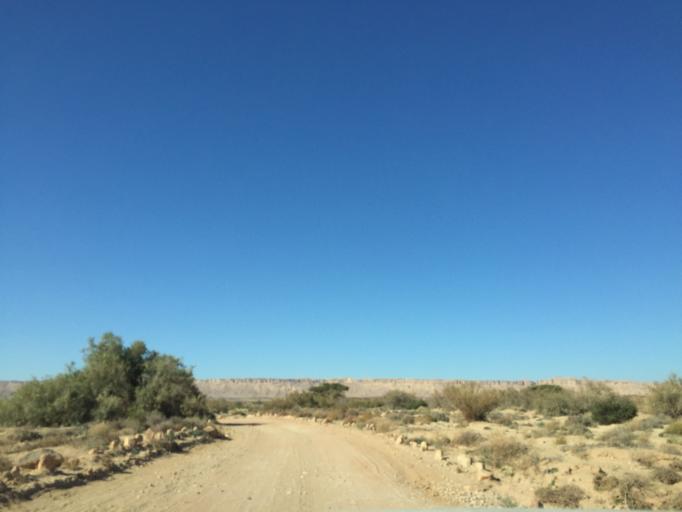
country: IL
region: Southern District
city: Mitzpe Ramon
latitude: 30.6221
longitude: 34.9290
